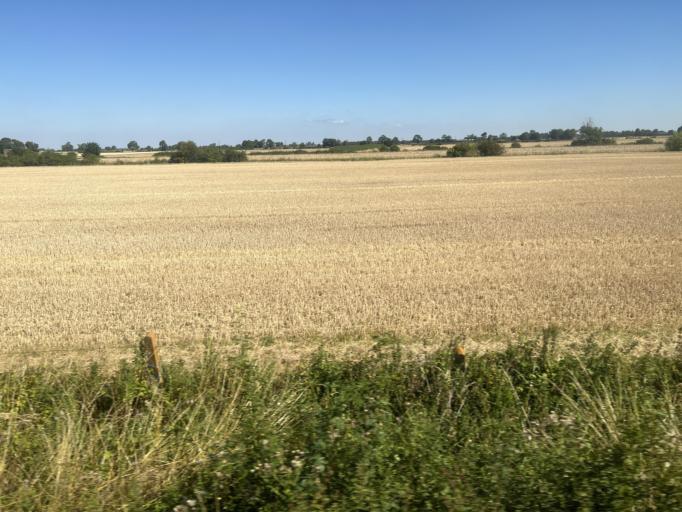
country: GB
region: England
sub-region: Lincolnshire
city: Heckington
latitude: 52.9687
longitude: -0.2470
